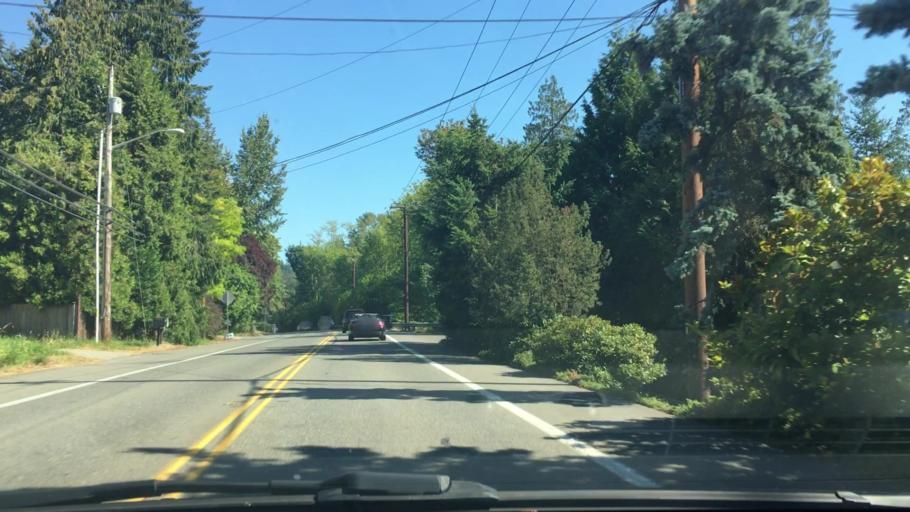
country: US
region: Washington
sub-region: King County
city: Sammamish
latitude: 47.6421
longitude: -122.0810
